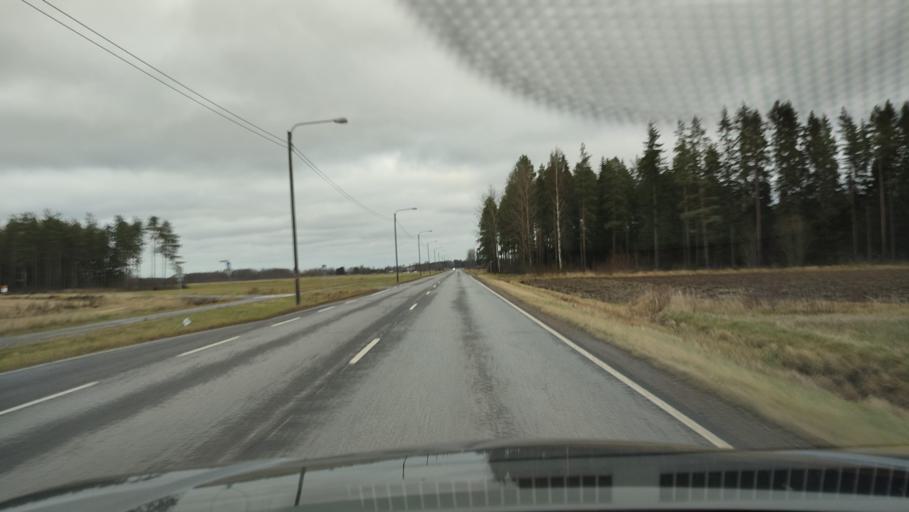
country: FI
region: Southern Ostrobothnia
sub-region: Seinaejoki
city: Kurikka
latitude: 62.6026
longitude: 22.4177
